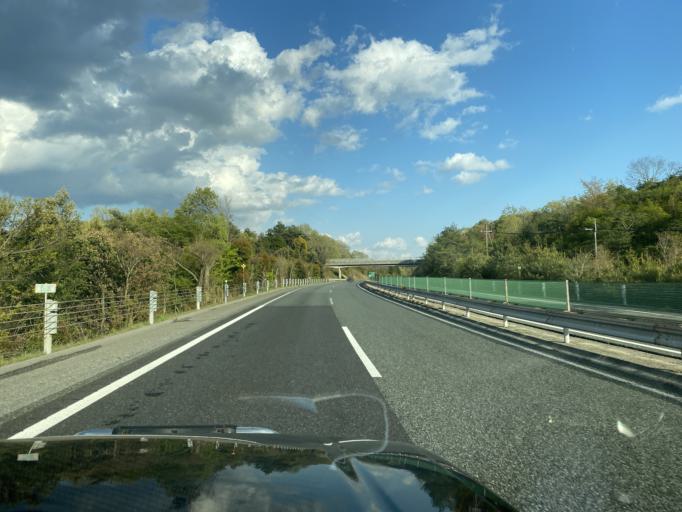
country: JP
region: Hyogo
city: Sandacho
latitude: 34.9421
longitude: 135.1537
